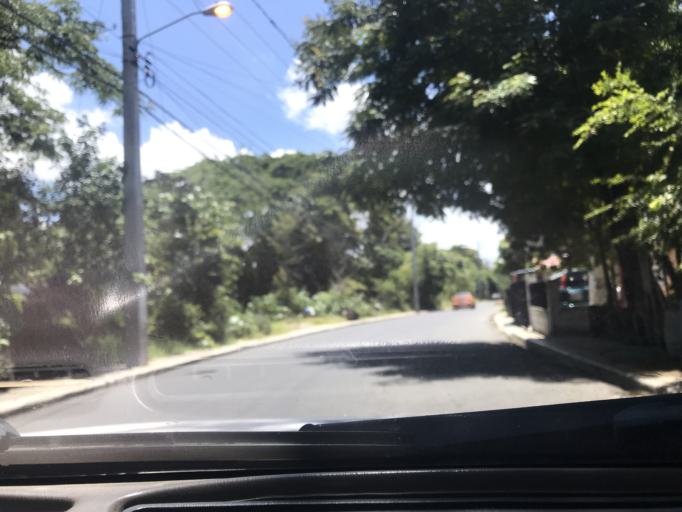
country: DO
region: Santiago
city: Santiago de los Caballeros
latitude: 19.4278
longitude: -70.7006
